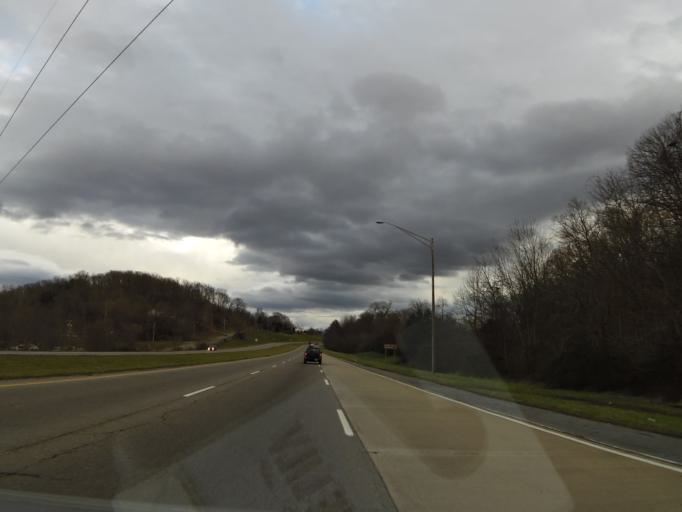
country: US
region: Tennessee
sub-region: Carter County
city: Pine Crest
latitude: 36.3113
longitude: -82.3273
